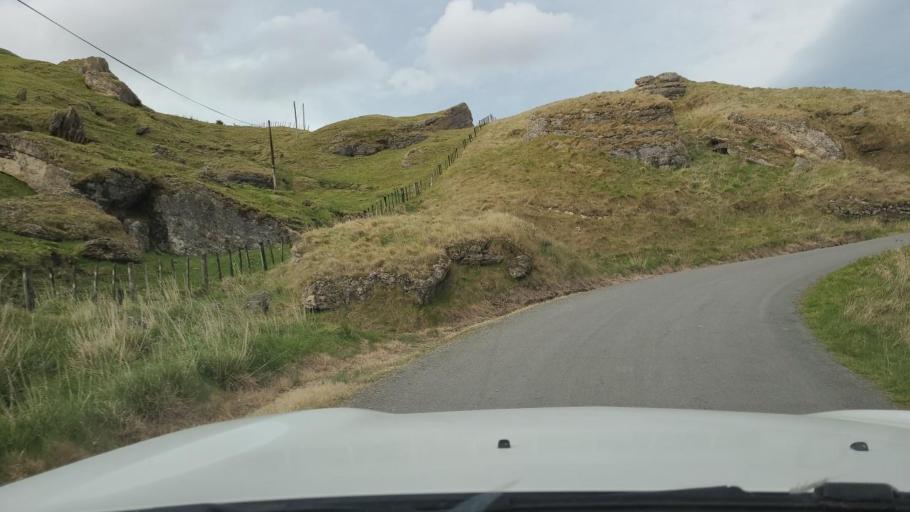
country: NZ
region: Hawke's Bay
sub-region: Napier City
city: Napier
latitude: -39.2037
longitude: 176.9419
